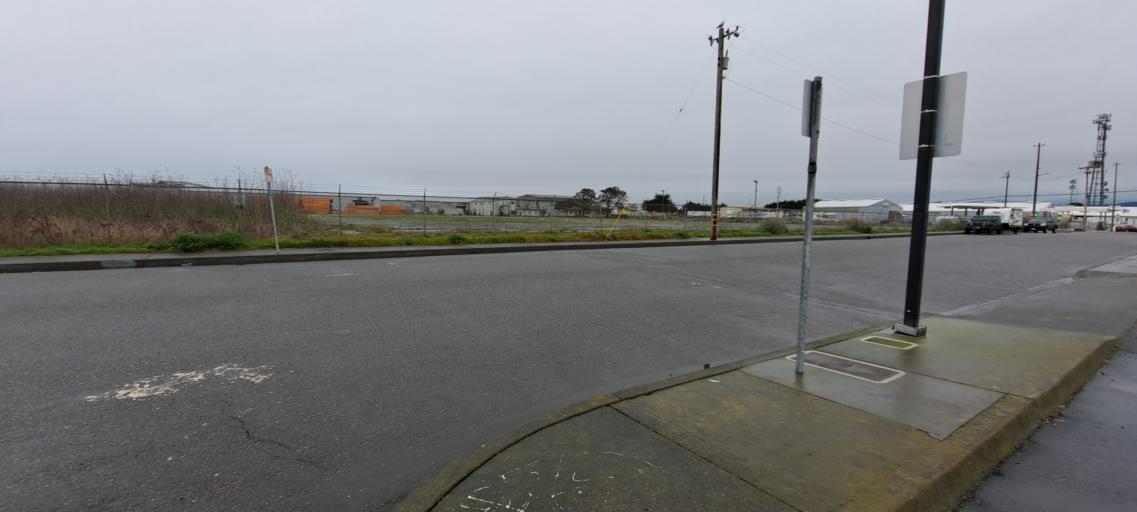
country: US
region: California
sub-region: Humboldt County
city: Bayview
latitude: 40.7906
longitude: -124.1866
